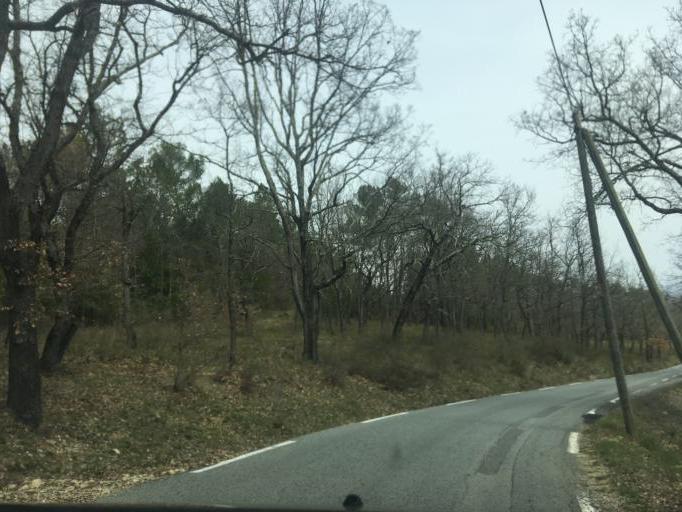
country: FR
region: Provence-Alpes-Cote d'Azur
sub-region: Departement du Var
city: Saint-Paul-en-Foret
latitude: 43.5807
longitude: 6.7260
